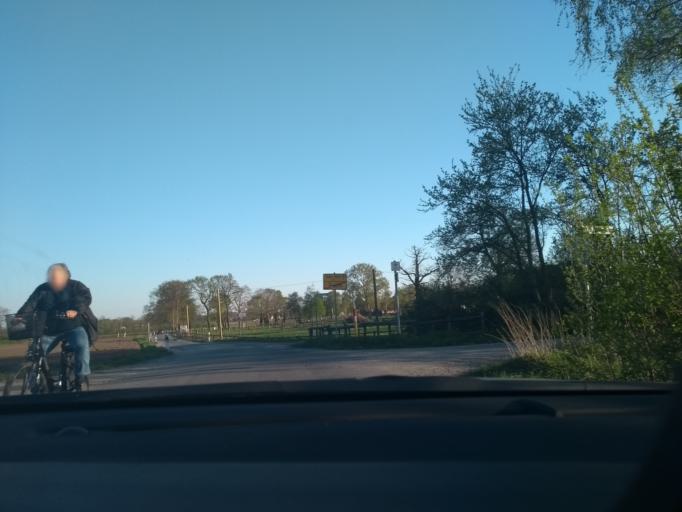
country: DE
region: North Rhine-Westphalia
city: Selm
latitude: 51.6849
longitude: 7.4643
